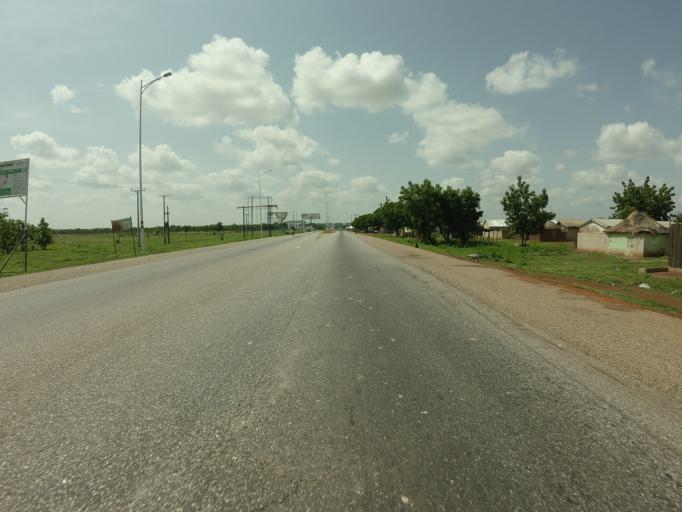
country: GH
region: Northern
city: Savelugu
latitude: 9.5498
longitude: -0.8378
